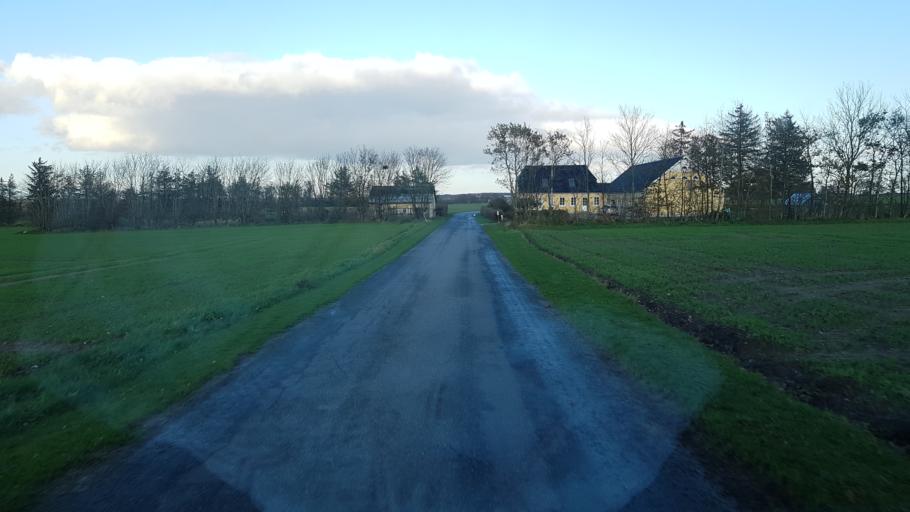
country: DK
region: South Denmark
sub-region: Vejen Kommune
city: Brorup
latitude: 55.4560
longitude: 8.9704
